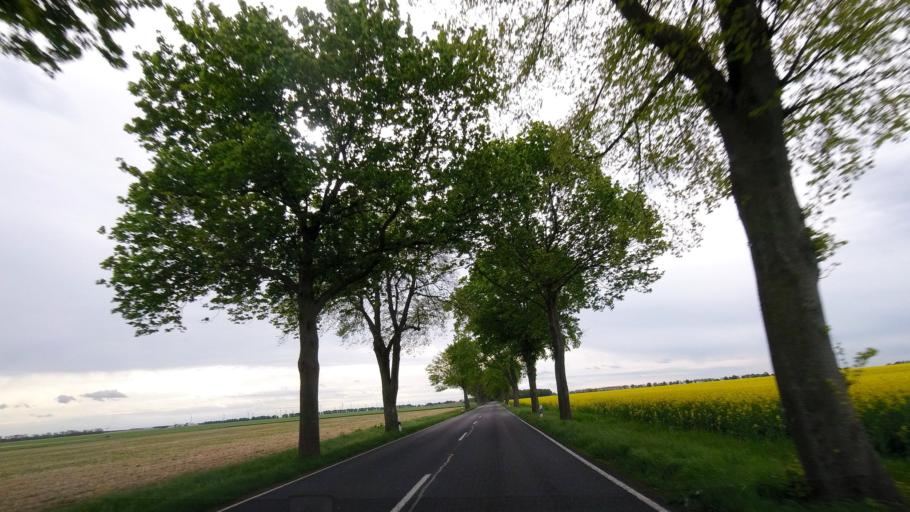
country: DE
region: Brandenburg
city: Ihlow
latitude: 51.9171
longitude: 13.2295
